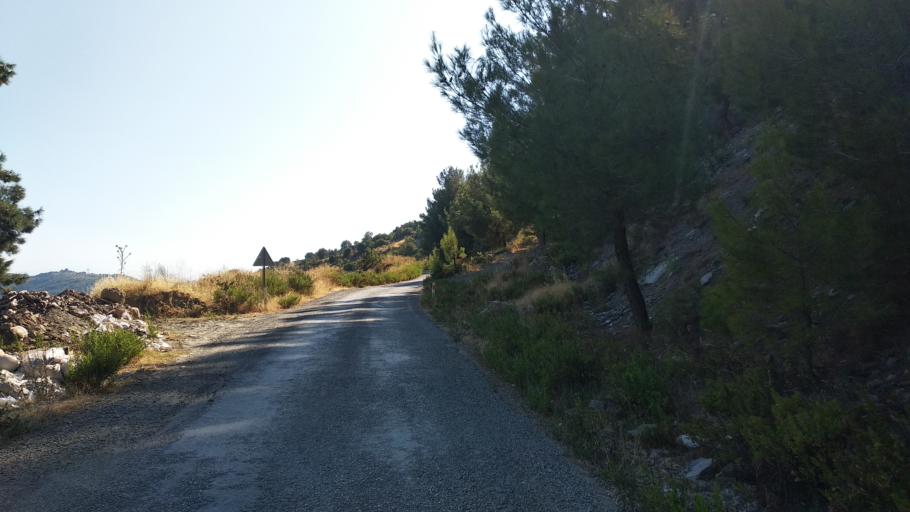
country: TR
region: Izmir
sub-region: Seferihisar
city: Seferhisar
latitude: 38.3224
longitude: 26.9316
